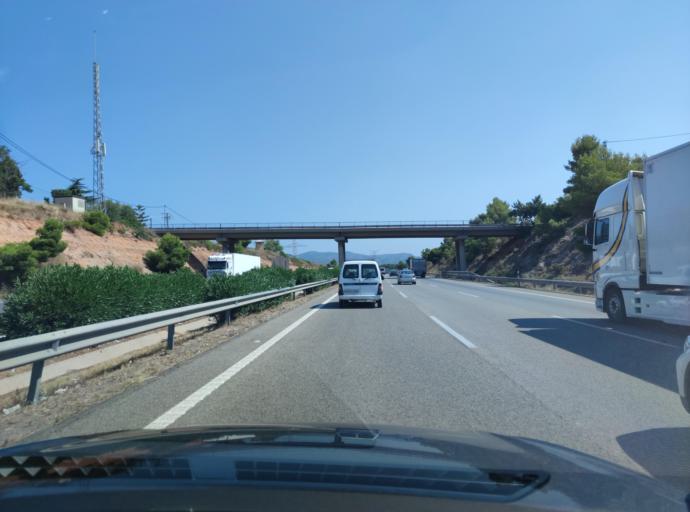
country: ES
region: Valencia
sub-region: Provincia de Valencia
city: Petres
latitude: 39.6640
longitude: -0.3041
